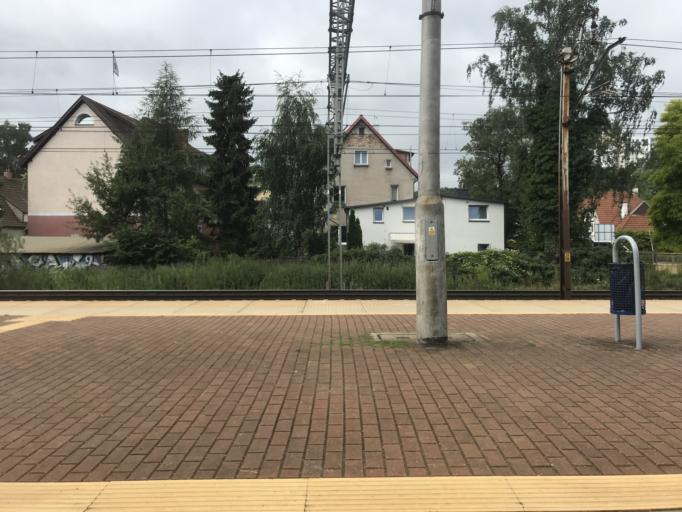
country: PL
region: Pomeranian Voivodeship
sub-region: Sopot
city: Sopot
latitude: 54.4570
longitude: 18.5537
